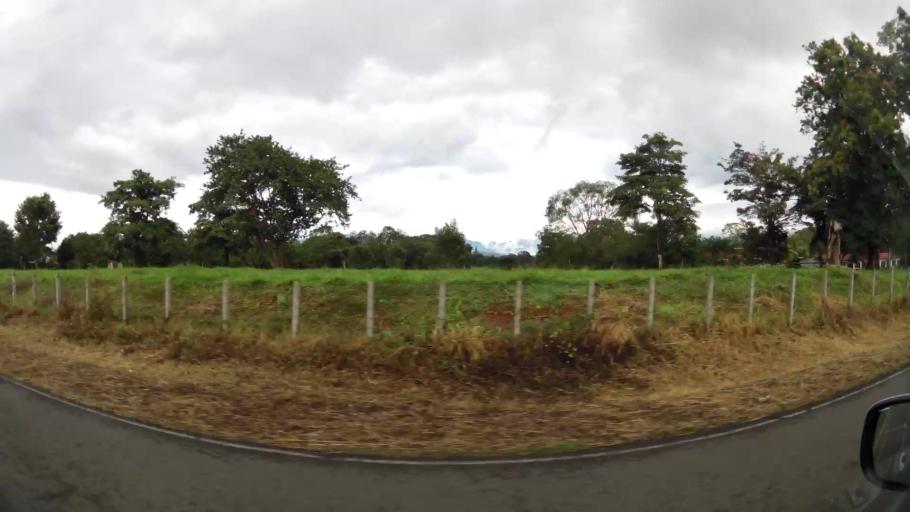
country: CR
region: Puntarenas
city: Esparza
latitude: 9.9945
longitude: -84.6492
